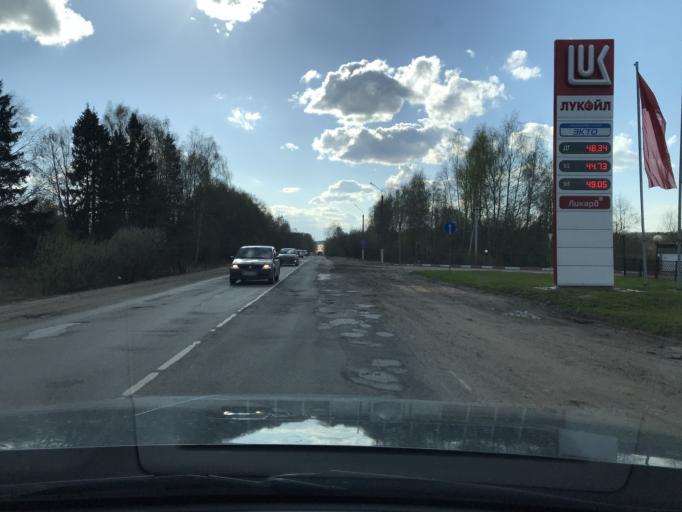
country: RU
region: Vladimir
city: Strunino
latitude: 56.4174
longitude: 38.5769
